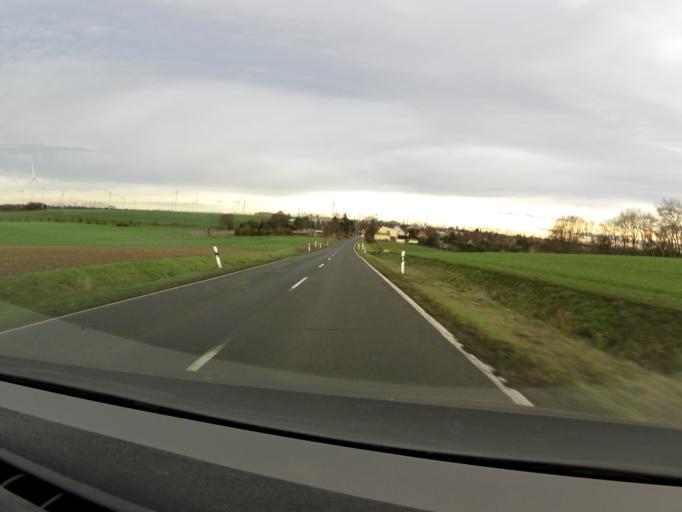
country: DE
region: Saxony-Anhalt
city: Gerbstedt
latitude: 51.6426
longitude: 11.6182
